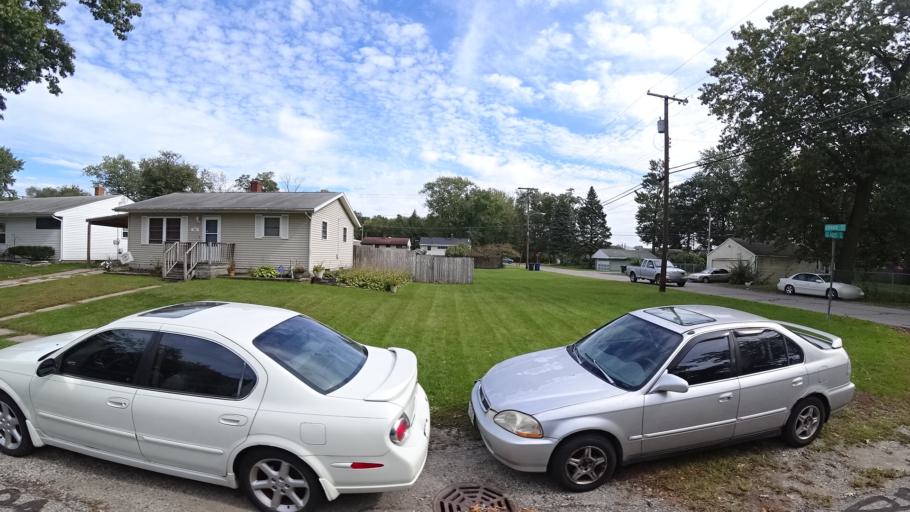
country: US
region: Indiana
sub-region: LaPorte County
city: Trail Creek
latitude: 41.7157
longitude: -86.8660
